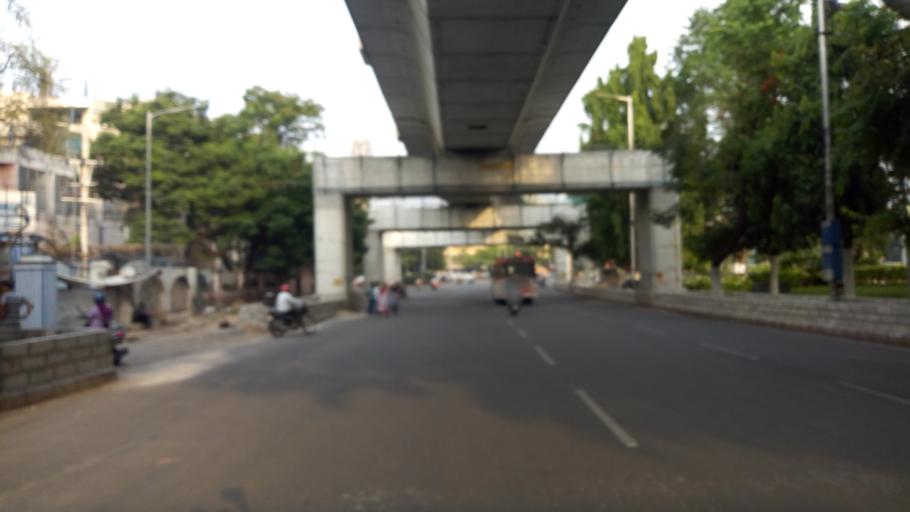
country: IN
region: Telangana
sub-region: Hyderabad
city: Hyderabad
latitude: 17.4015
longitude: 78.4689
